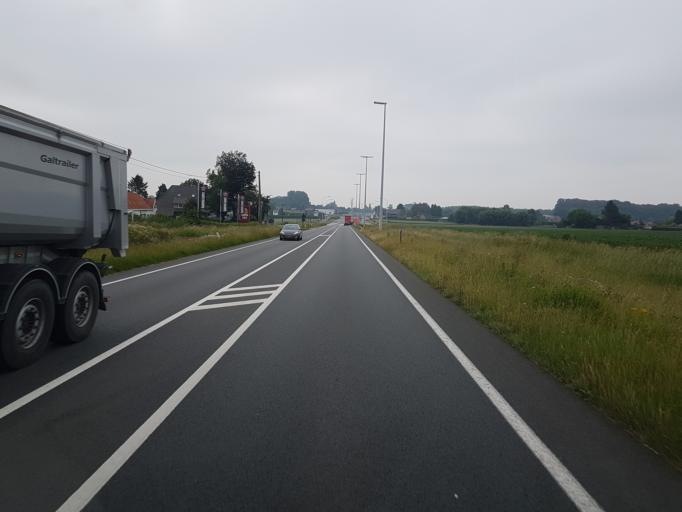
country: BE
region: Flanders
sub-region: Provincie Oost-Vlaanderen
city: Zottegem
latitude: 50.9036
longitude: 3.8251
